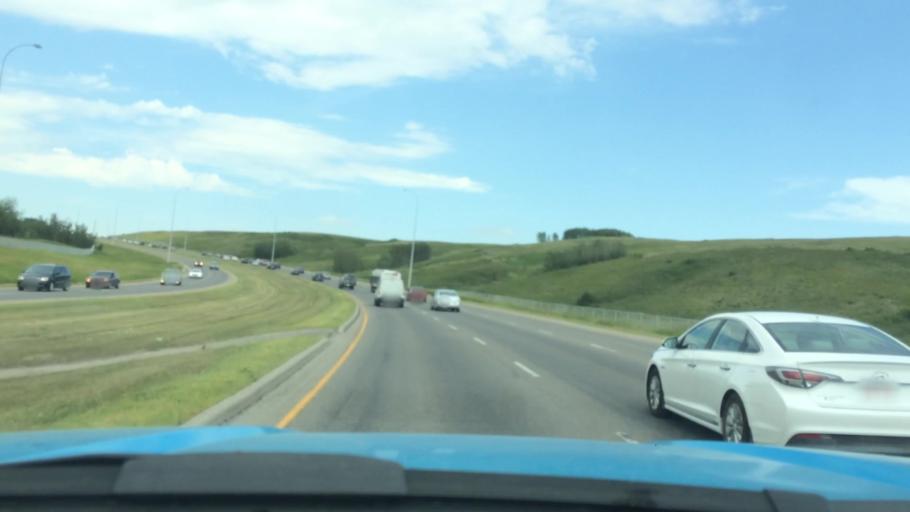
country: CA
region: Alberta
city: Calgary
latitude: 51.1148
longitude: -114.1345
